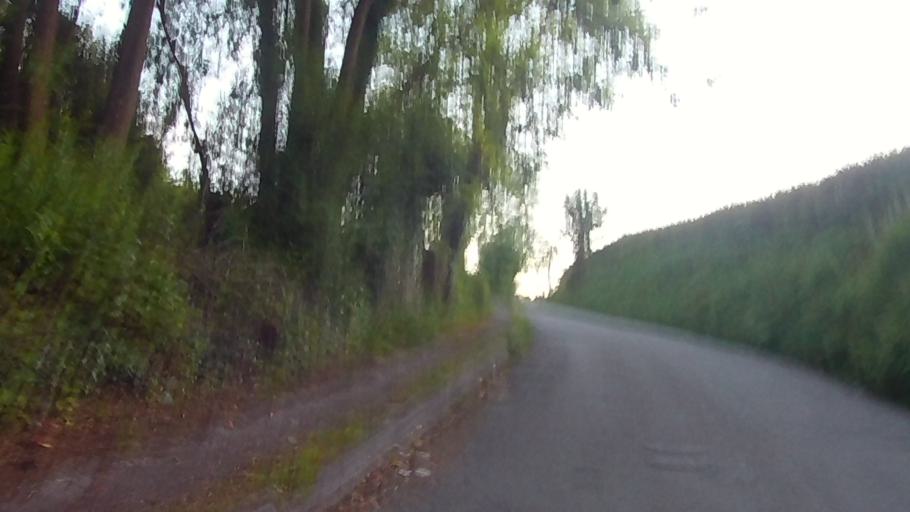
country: IE
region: Munster
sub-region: County Cork
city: Midleton
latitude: 51.9731
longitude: -8.2180
